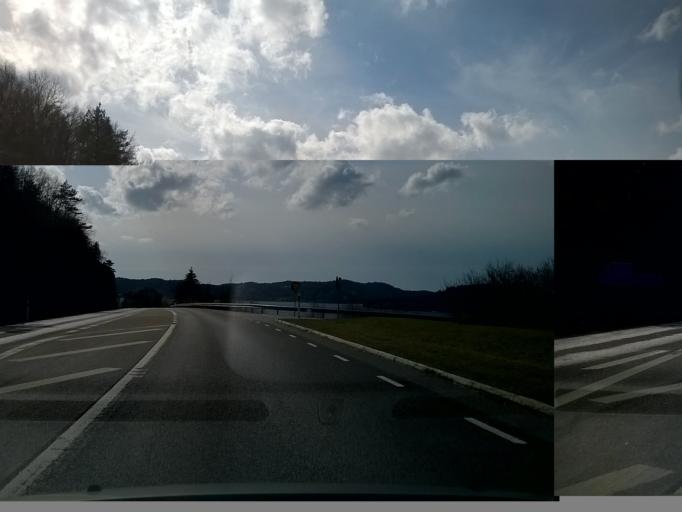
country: SE
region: Vaestra Goetaland
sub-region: Orust
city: Henan
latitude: 58.2622
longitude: 11.6800
